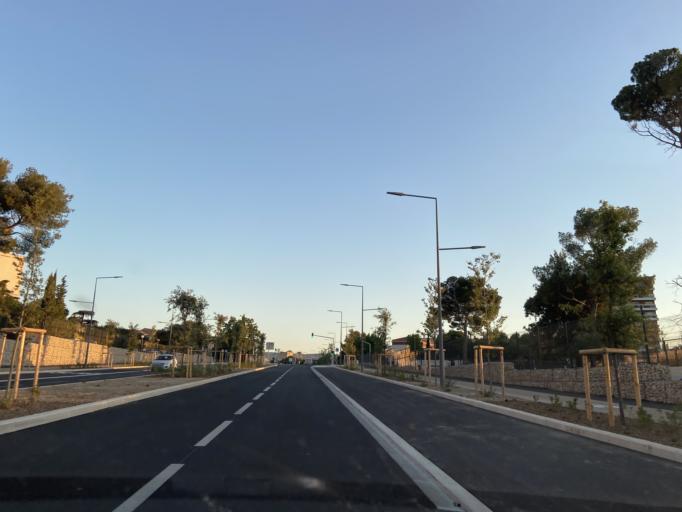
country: FR
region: Provence-Alpes-Cote d'Azur
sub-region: Departement des Bouches-du-Rhone
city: Marseille 10
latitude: 43.2725
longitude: 5.4229
